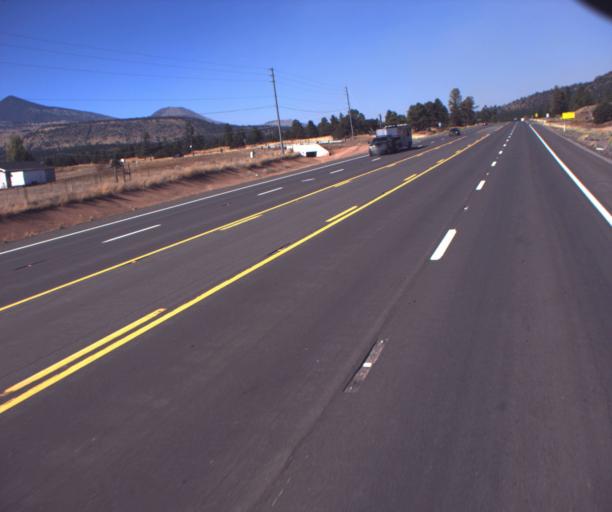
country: US
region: Arizona
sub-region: Coconino County
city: Flagstaff
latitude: 35.3269
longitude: -111.5445
